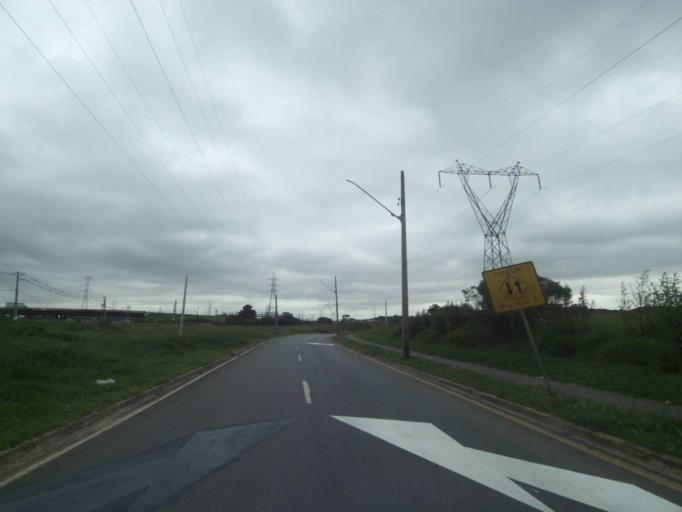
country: BR
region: Parana
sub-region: Araucaria
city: Araucaria
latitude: -25.5212
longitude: -49.3353
